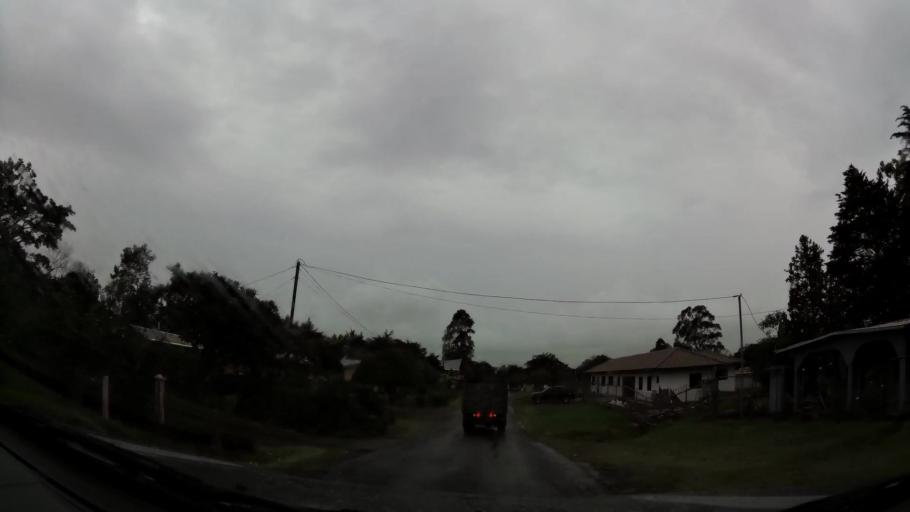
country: PA
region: Chiriqui
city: Volcan
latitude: 8.7887
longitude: -82.6497
